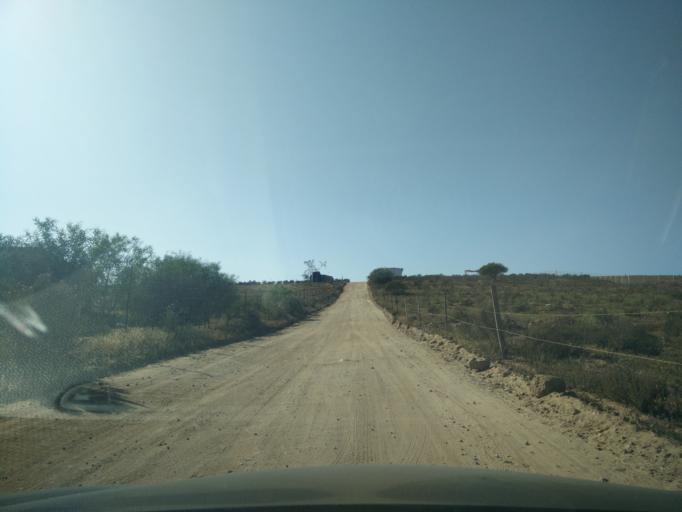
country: MX
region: Baja California
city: El Sauzal
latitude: 32.0184
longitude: -116.6659
